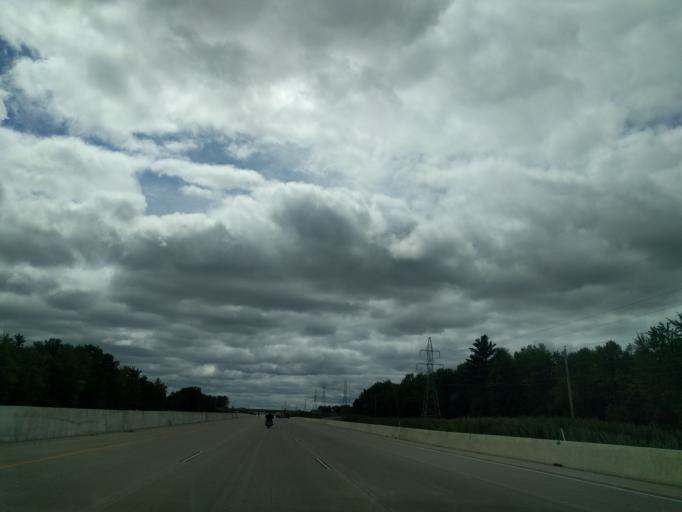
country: US
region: Wisconsin
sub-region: Brown County
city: Suamico
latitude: 44.5820
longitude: -88.0487
